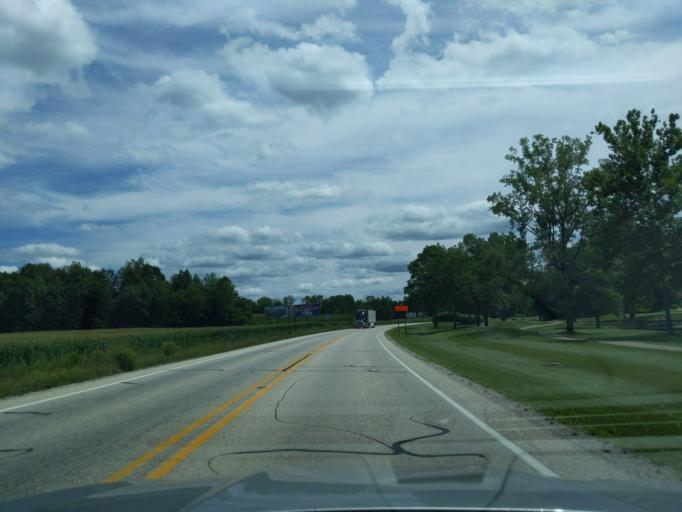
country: US
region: Indiana
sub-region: Ripley County
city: Batesville
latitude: 39.3101
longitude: -85.2286
